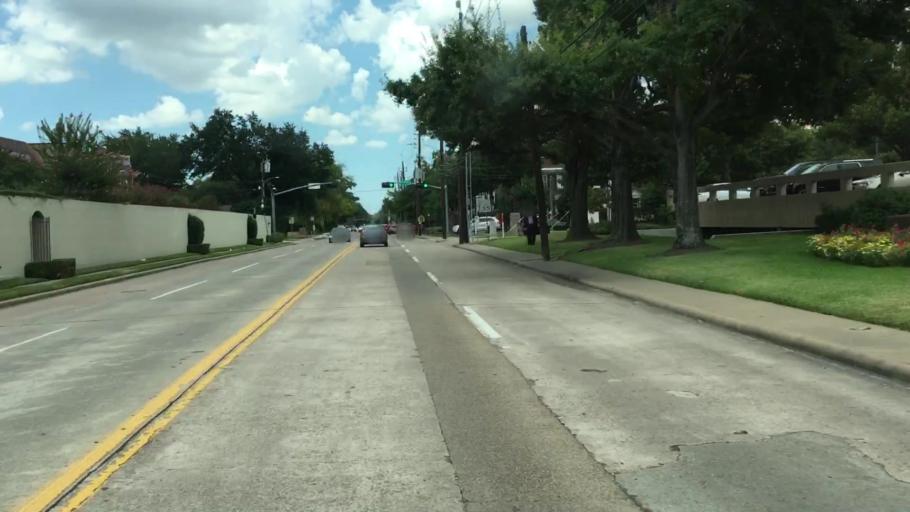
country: US
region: Texas
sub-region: Harris County
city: Hunters Creek Village
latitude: 29.7454
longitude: -95.4670
